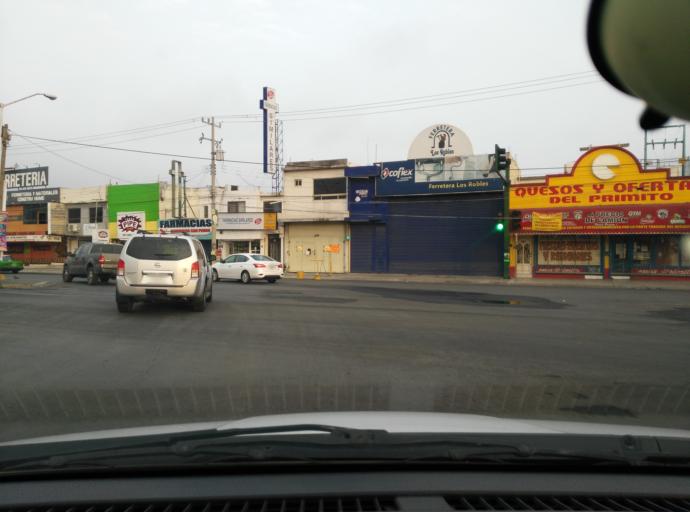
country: MX
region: Nuevo Leon
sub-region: San Nicolas de los Garza
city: San Nicolas de los Garza
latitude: 25.7725
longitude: -100.2608
